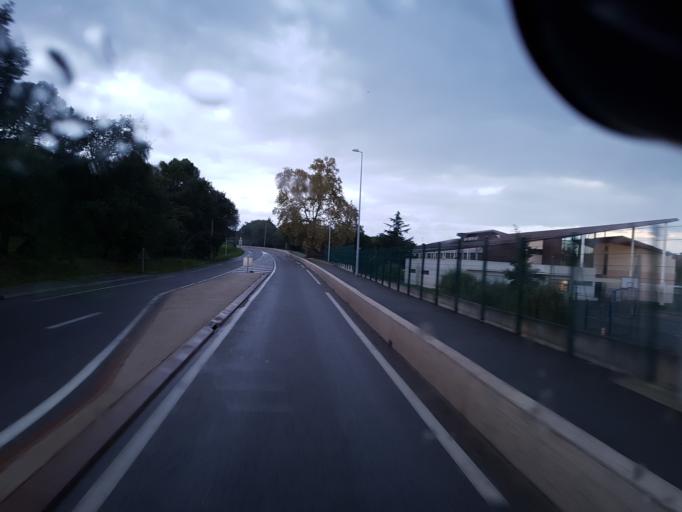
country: FR
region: Provence-Alpes-Cote d'Azur
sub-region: Departement du Var
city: Gassin
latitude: 43.2451
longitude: 6.5711
